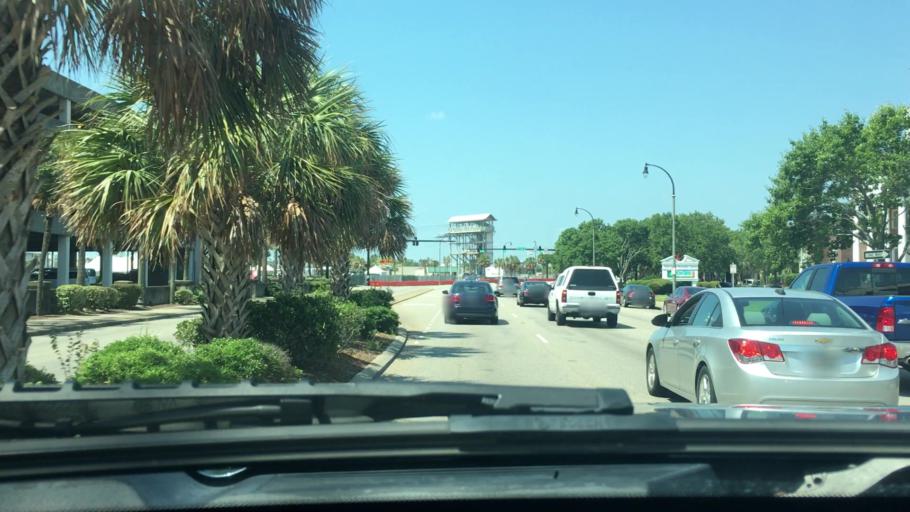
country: US
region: South Carolina
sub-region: Horry County
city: Myrtle Beach
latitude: 33.6946
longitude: -78.8813
